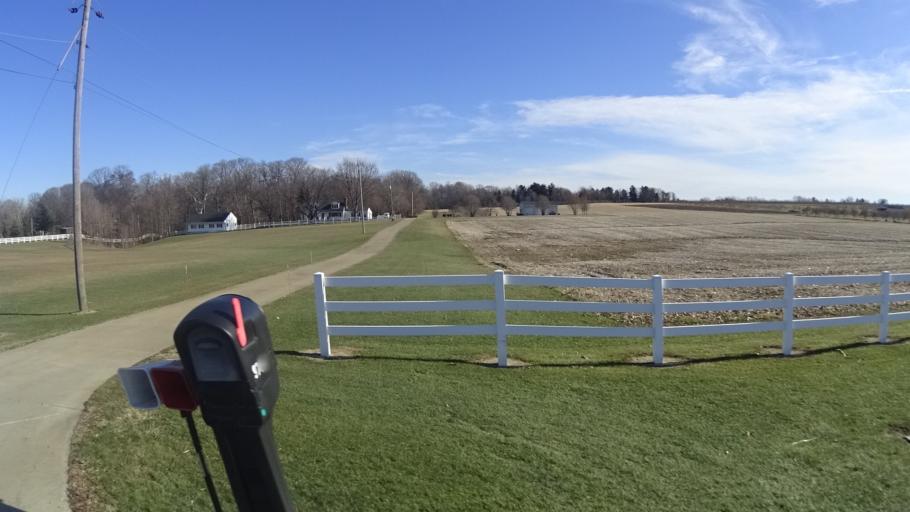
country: US
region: Ohio
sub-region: Lorain County
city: South Amherst
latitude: 41.3496
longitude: -82.2994
